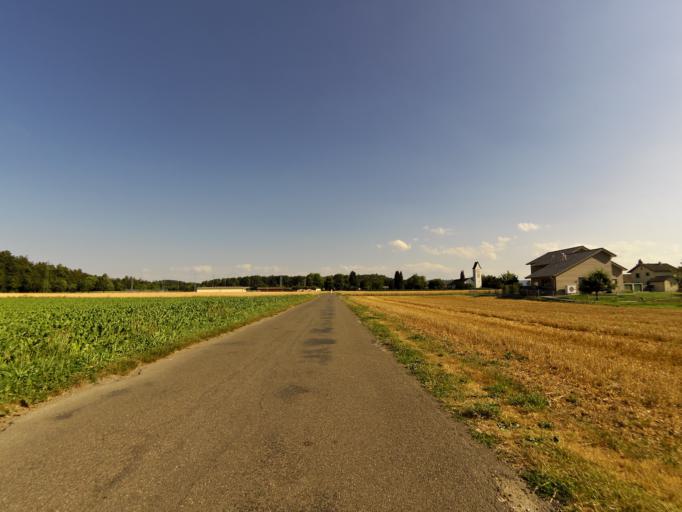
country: CH
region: Aargau
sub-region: Bezirk Lenzburg
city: Niederlenz
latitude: 47.4044
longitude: 8.1802
